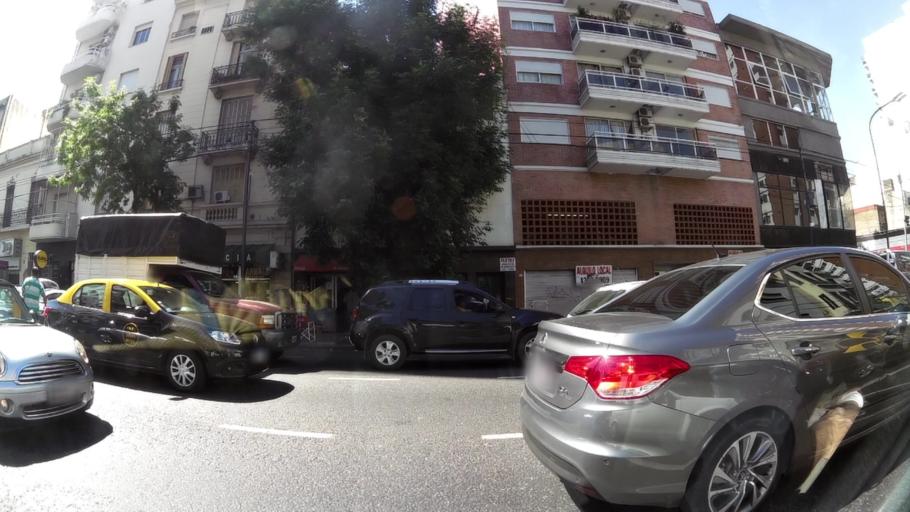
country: AR
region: Buenos Aires F.D.
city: Buenos Aires
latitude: -34.6230
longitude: -58.3968
